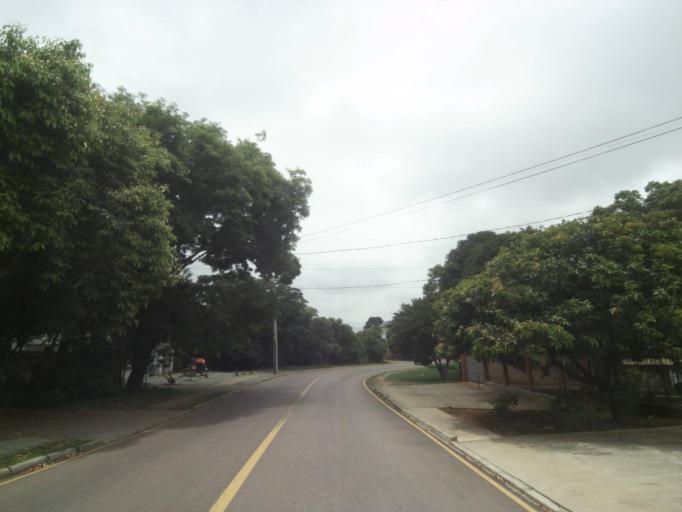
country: BR
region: Parana
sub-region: Curitiba
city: Curitiba
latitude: -25.4815
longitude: -49.3417
